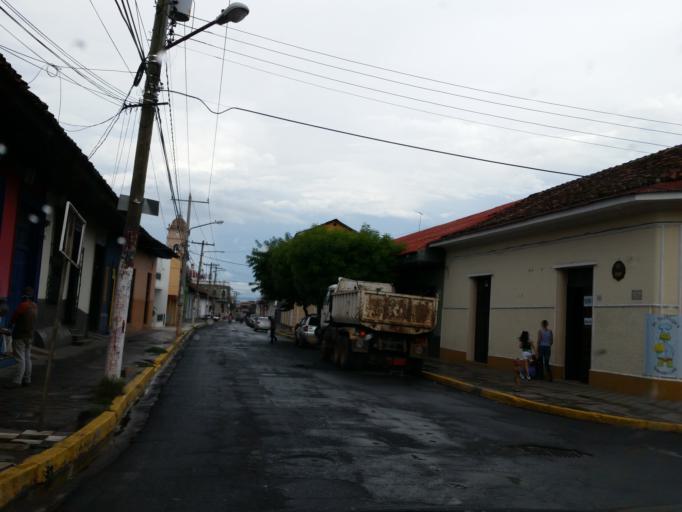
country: NI
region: Granada
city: Granada
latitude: 11.9290
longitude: -85.9588
